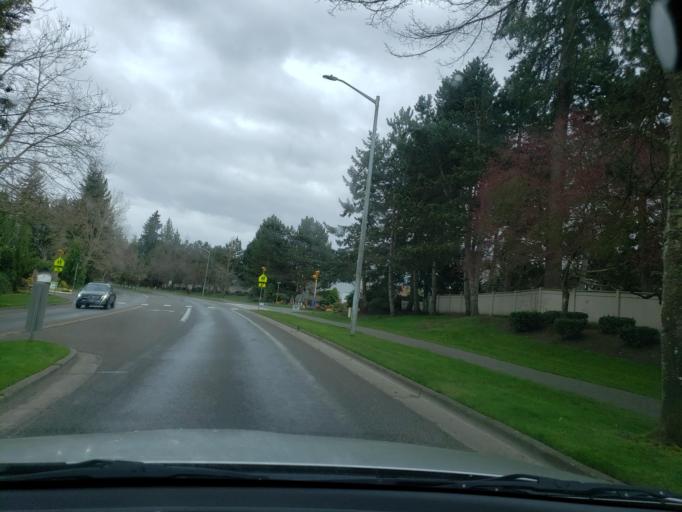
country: US
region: Washington
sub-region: Snohomish County
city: Meadowdale
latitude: 47.8866
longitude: -122.3089
